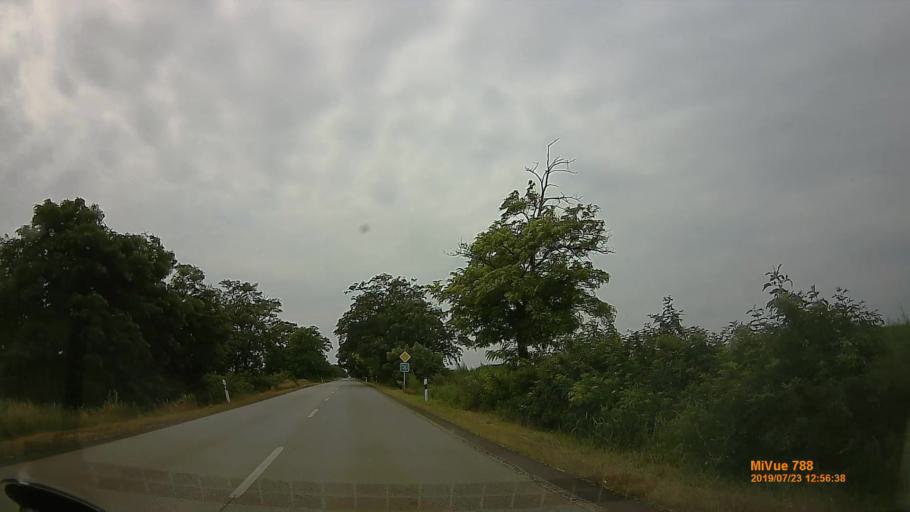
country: HU
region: Szabolcs-Szatmar-Bereg
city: Nagycserkesz
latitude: 47.9573
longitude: 21.4955
